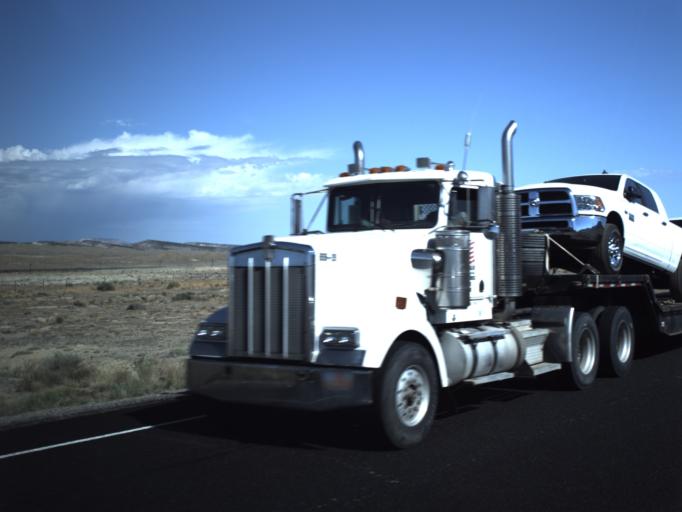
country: US
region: Utah
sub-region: Carbon County
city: East Carbon City
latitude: 39.1790
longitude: -110.3383
